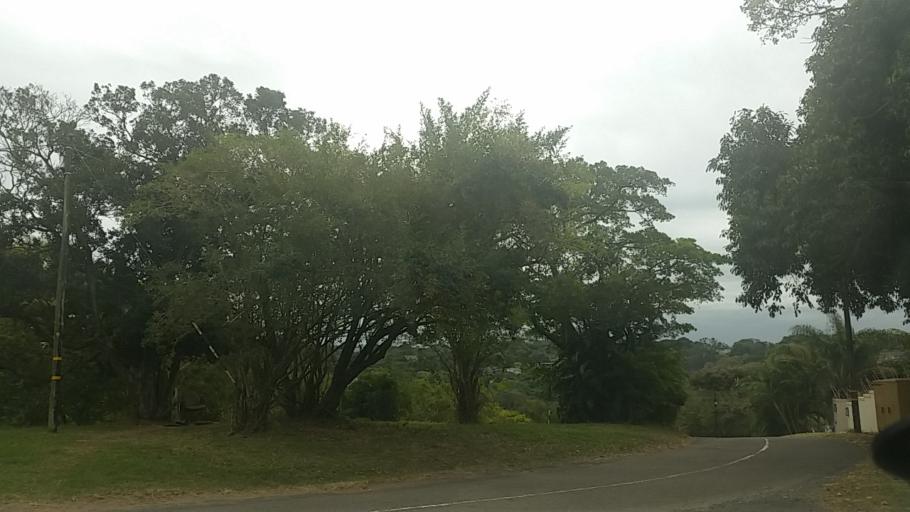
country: ZA
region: KwaZulu-Natal
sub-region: eThekwini Metropolitan Municipality
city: Berea
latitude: -29.8429
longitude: 30.9311
